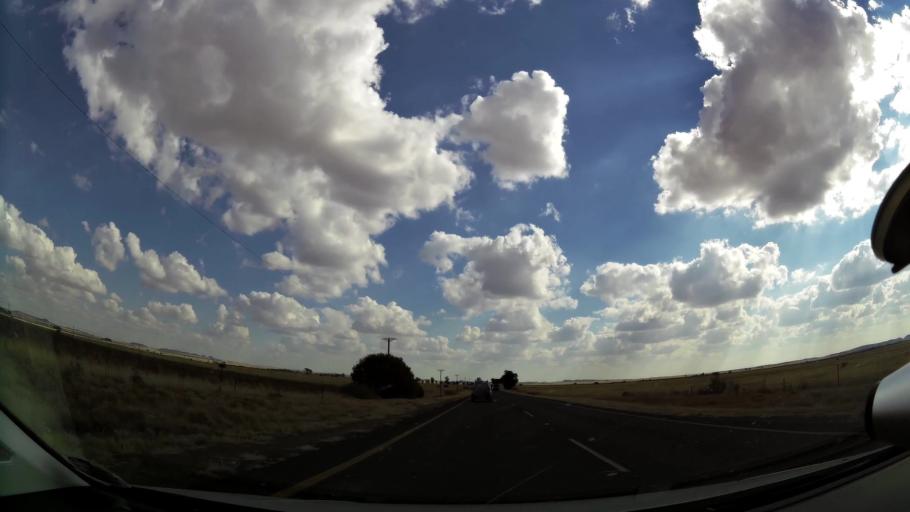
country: ZA
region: Orange Free State
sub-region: Xhariep District Municipality
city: Koffiefontein
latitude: -29.1321
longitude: 25.5379
